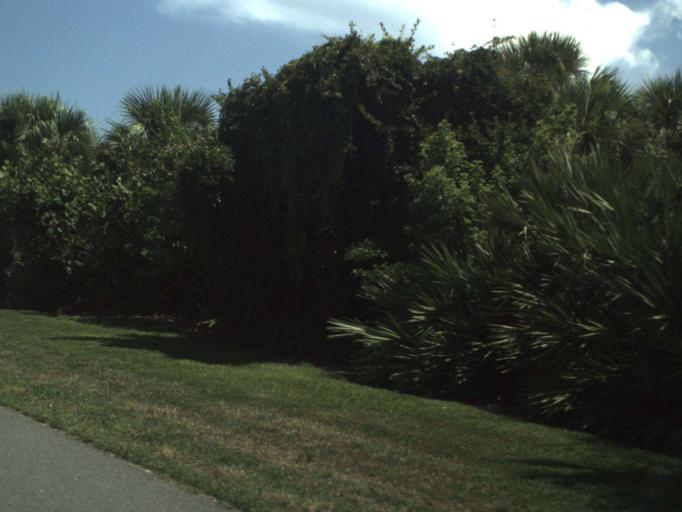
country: US
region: Florida
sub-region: Saint Lucie County
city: Fort Pierce North
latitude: 27.5264
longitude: -80.3129
